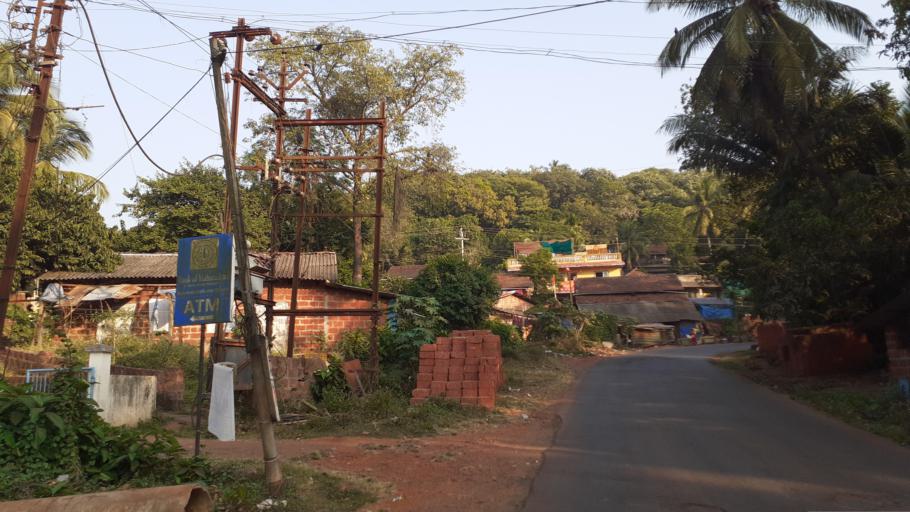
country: IN
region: Maharashtra
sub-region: Ratnagiri
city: Ratnagiri
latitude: 17.0438
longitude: 73.2973
